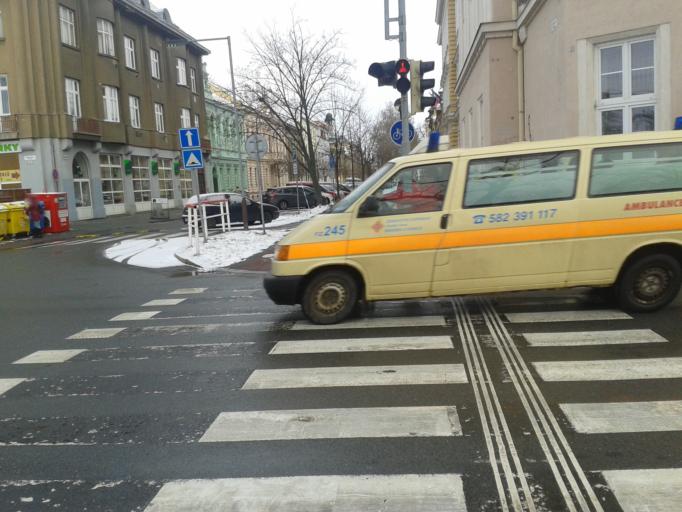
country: CZ
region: Olomoucky
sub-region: Okres Prostejov
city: Prostejov
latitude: 49.4742
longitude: 17.1098
